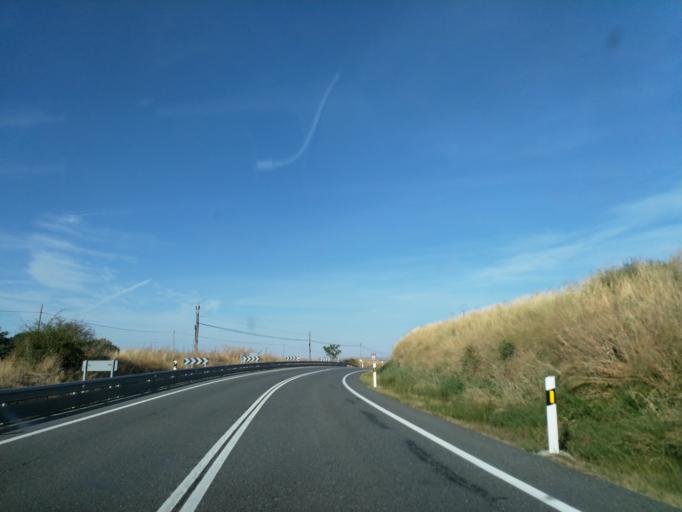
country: ES
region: Castille and Leon
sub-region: Provincia de Segovia
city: Villacastin
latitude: 40.7860
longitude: -4.4049
